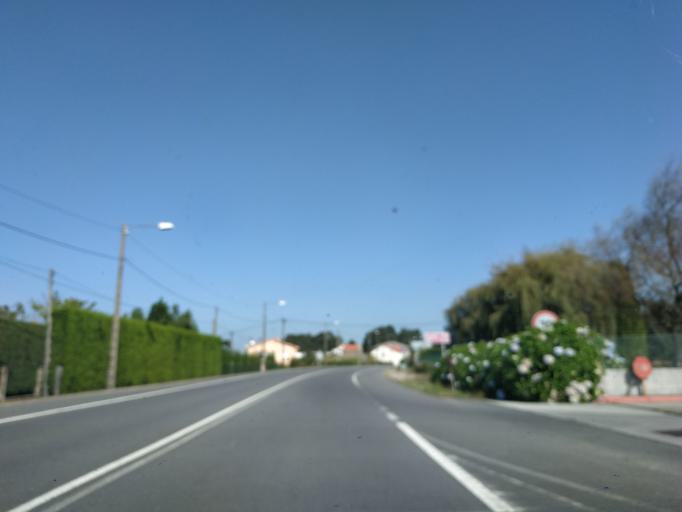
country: ES
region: Galicia
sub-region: Provincia da Coruna
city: Laracha
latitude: 43.2508
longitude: -8.6144
